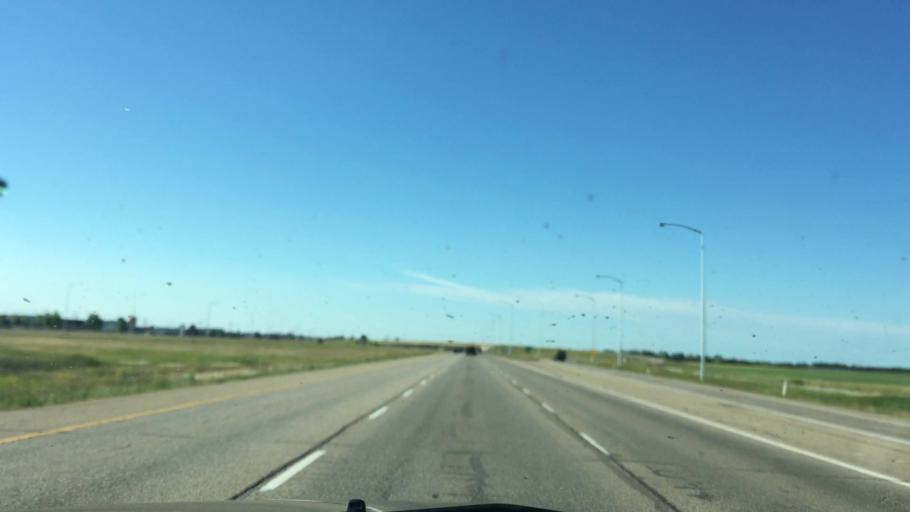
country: CA
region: Alberta
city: Leduc
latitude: 53.2922
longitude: -113.5499
